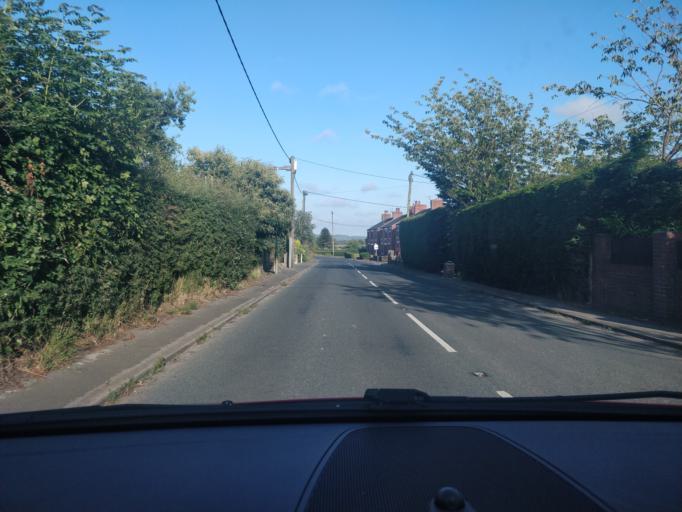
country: GB
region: England
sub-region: Lancashire
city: Tarleton
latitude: 53.6451
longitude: -2.8630
